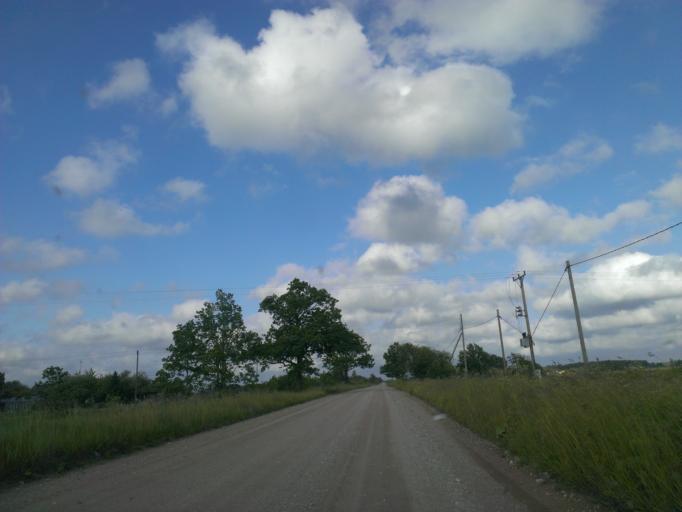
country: LV
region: Aizpute
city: Aizpute
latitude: 56.7513
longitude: 21.4186
